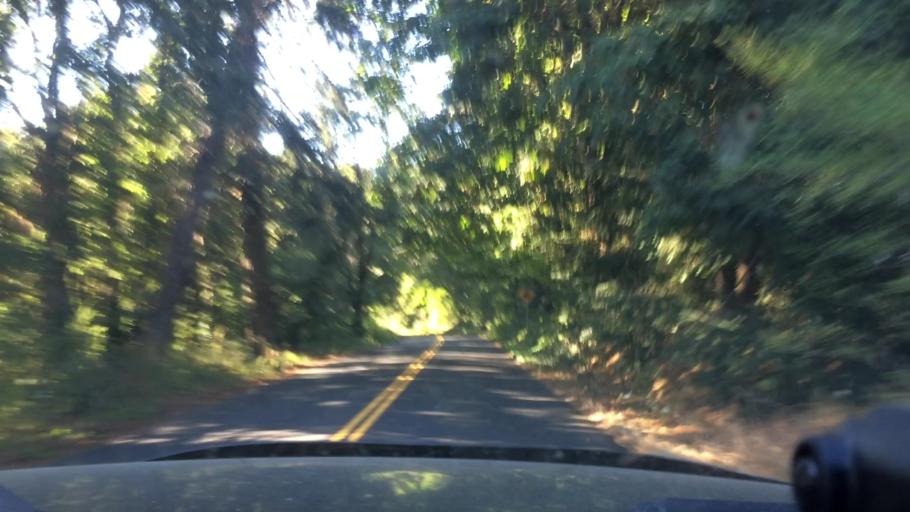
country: US
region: Oregon
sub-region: Yamhill County
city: Newberg
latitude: 45.3310
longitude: -122.9395
